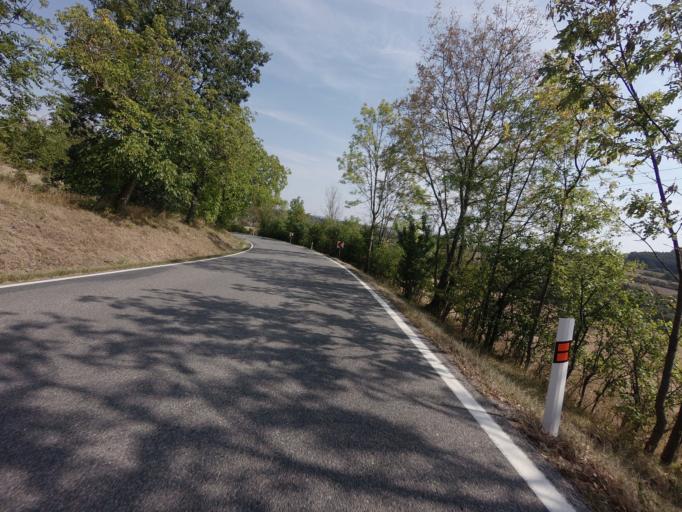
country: CZ
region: Central Bohemia
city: Petrovice
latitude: 49.5884
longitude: 14.3837
